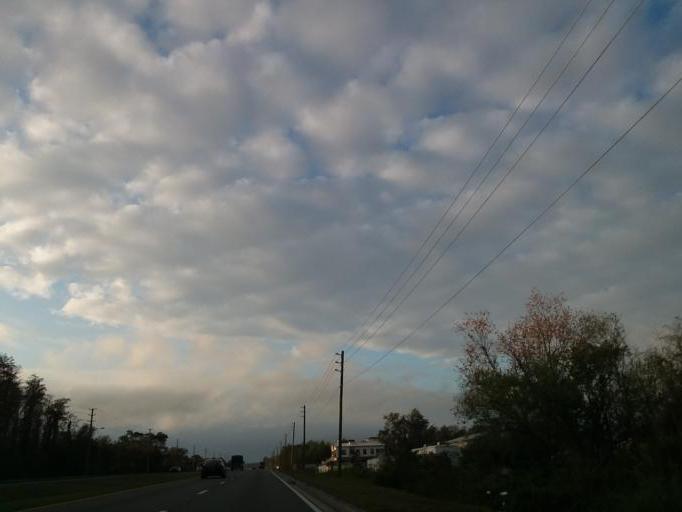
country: US
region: Florida
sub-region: Osceola County
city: Campbell
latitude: 28.2198
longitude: -81.4404
